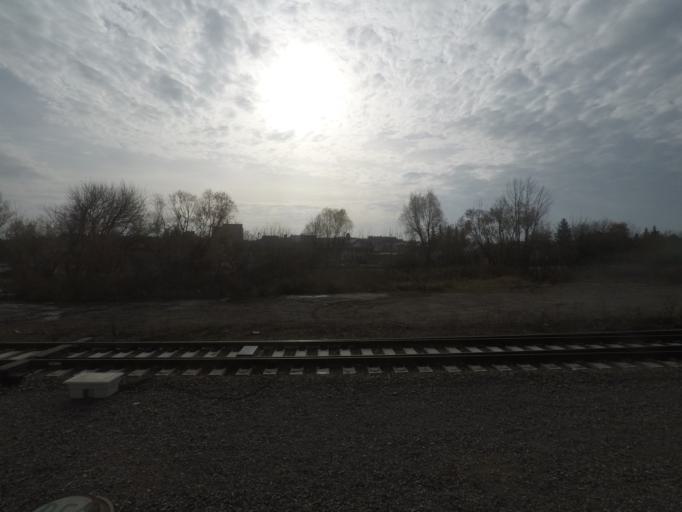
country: PL
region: Subcarpathian Voivodeship
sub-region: Powiat ropczycko-sedziszowski
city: Sedziszow Malopolski
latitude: 50.0750
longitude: 21.7010
